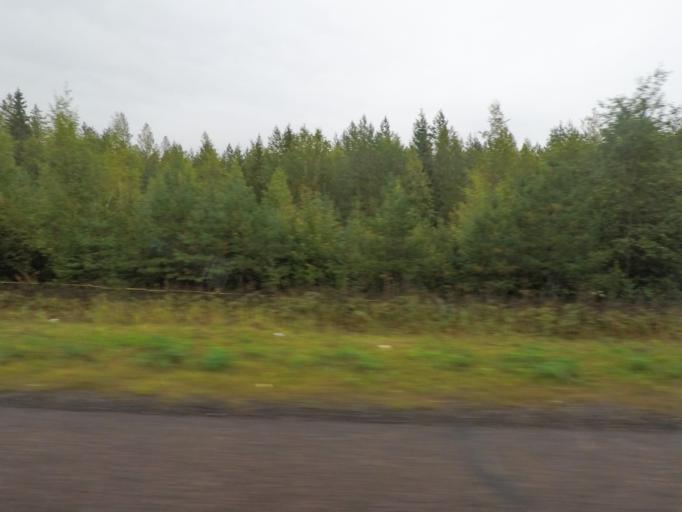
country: FI
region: Northern Savo
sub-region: Varkaus
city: Leppaevirta
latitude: 62.4268
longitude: 27.8155
